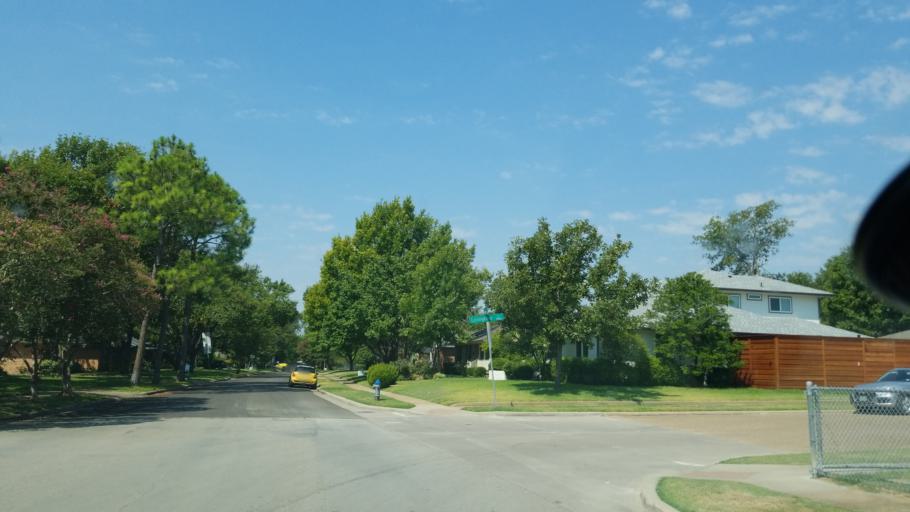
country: US
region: Texas
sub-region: Dallas County
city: Richardson
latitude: 32.8751
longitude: -96.7104
